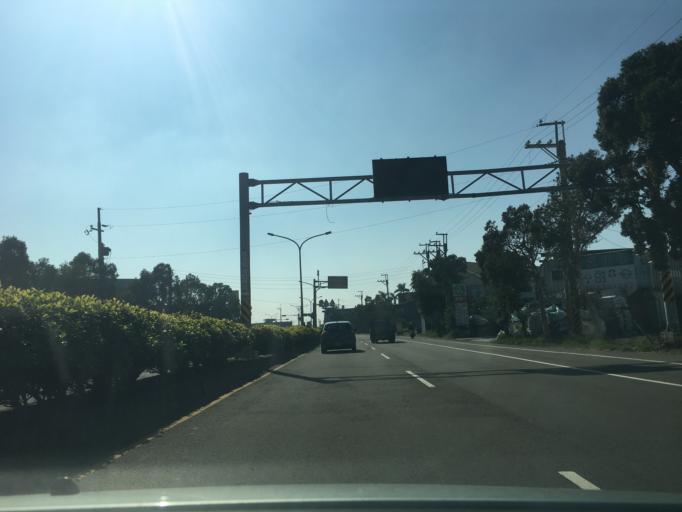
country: TW
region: Taiwan
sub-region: Hsinchu
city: Hsinchu
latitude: 24.8198
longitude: 120.9258
